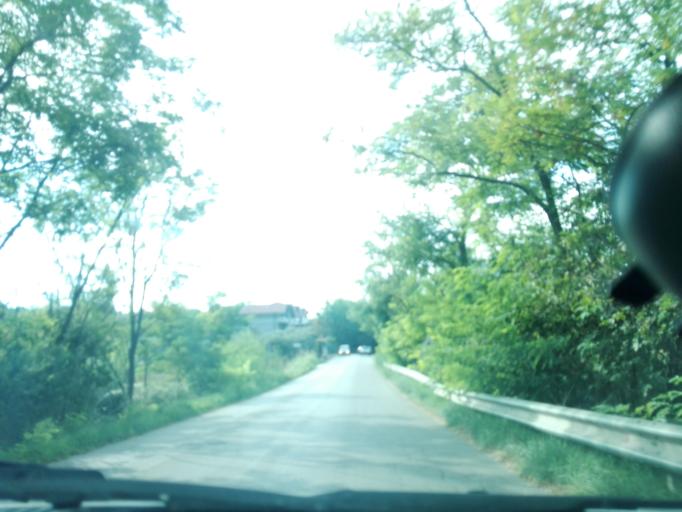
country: IT
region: Abruzzo
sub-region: Provincia di Pescara
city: Cappelle sul Tavo
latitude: 42.4584
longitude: 14.1109
